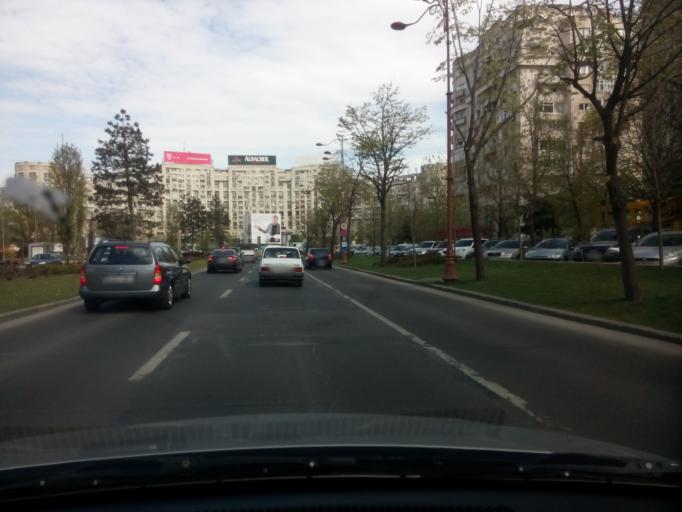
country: RO
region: Bucuresti
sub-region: Municipiul Bucuresti
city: Bucharest
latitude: 44.4256
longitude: 26.1265
